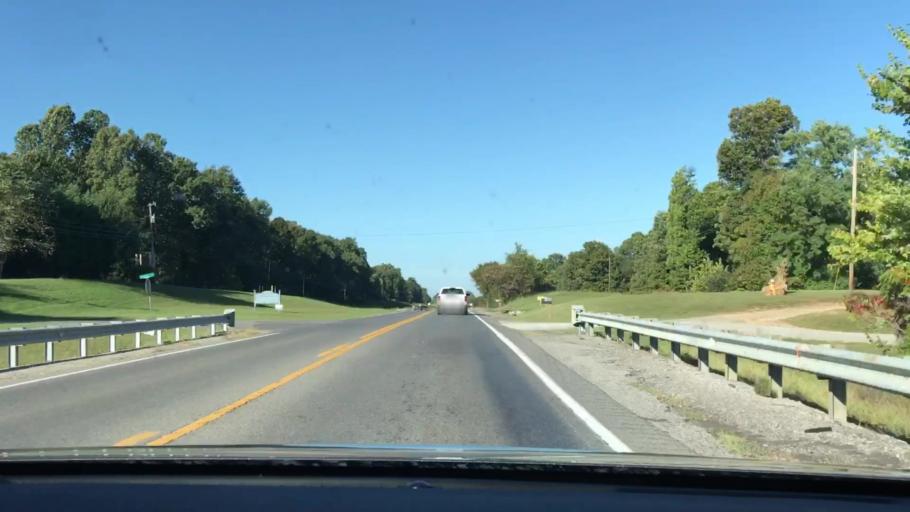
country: US
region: Kentucky
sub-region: Marshall County
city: Calvert City
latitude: 37.0046
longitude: -88.3722
